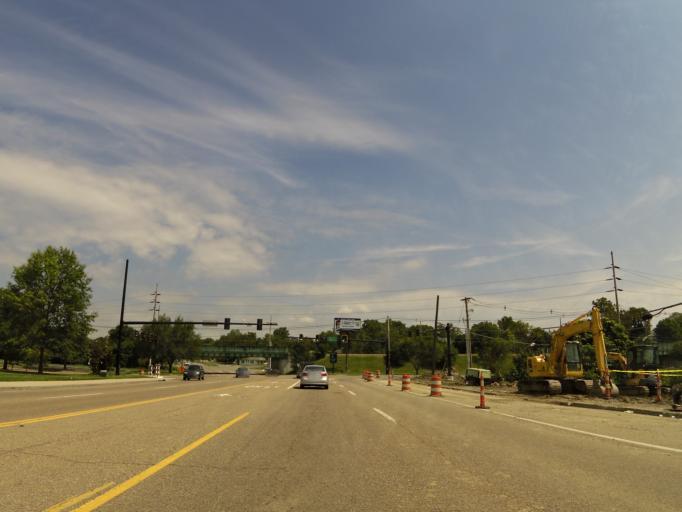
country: US
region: Tennessee
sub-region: Sullivan County
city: Kingsport
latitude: 36.5352
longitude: -82.5497
